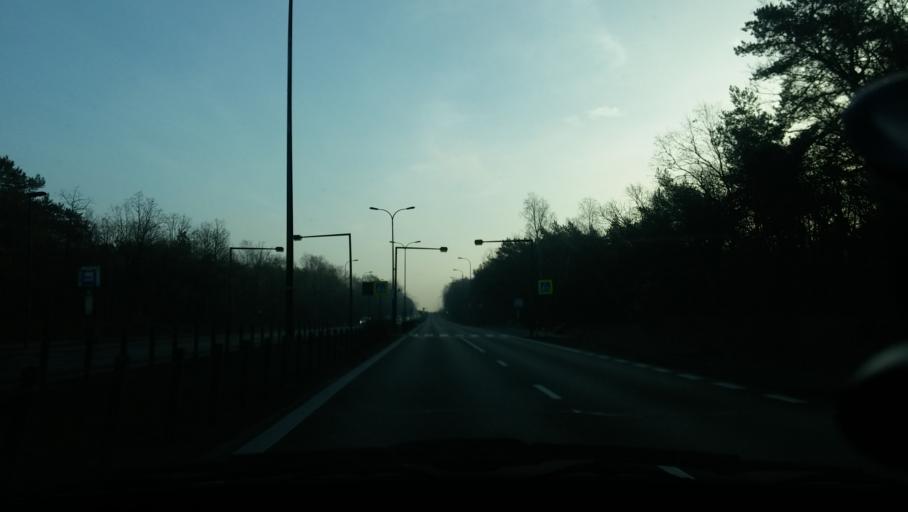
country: PL
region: Masovian Voivodeship
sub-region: Warszawa
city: Wesola
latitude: 52.2242
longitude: 21.2055
